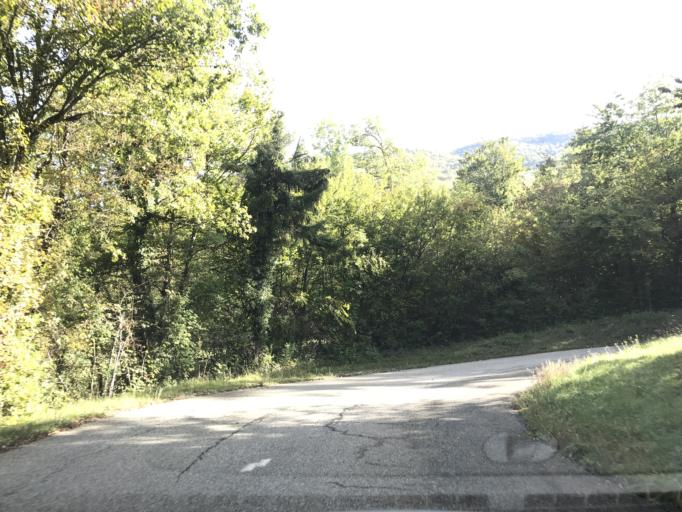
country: FR
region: Rhone-Alpes
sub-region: Departement de la Savoie
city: Novalaise
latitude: 45.6448
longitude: 5.7945
